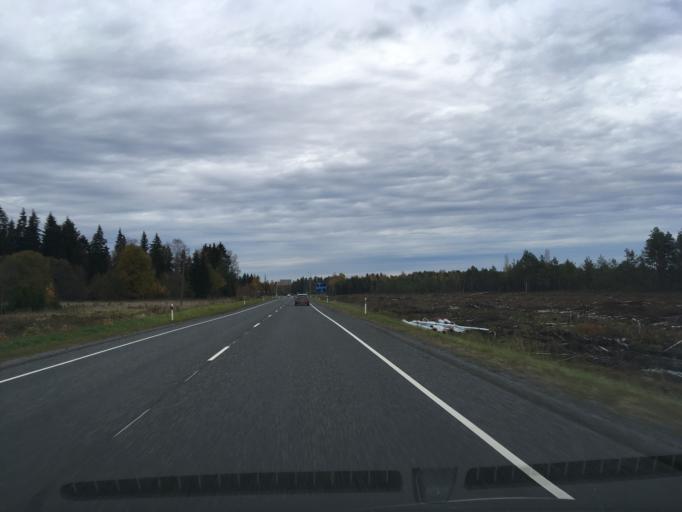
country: EE
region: Harju
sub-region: Nissi vald
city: Turba
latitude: 58.9886
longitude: 24.0582
